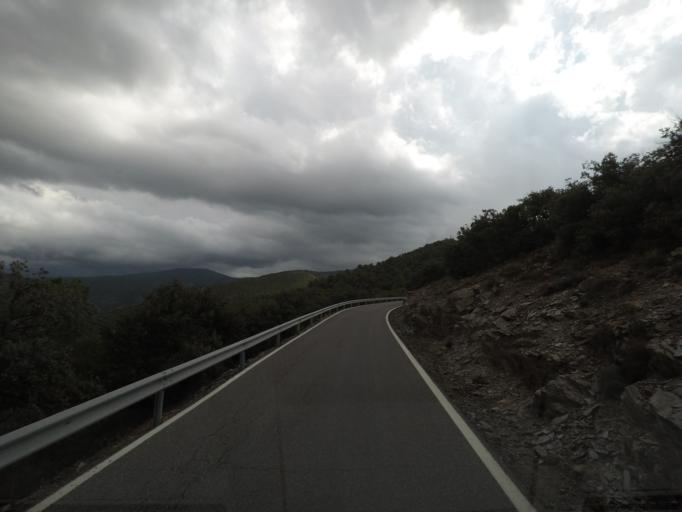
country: ES
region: Andalusia
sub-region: Provincia de Granada
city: Ferreira
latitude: 37.1573
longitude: -3.0505
